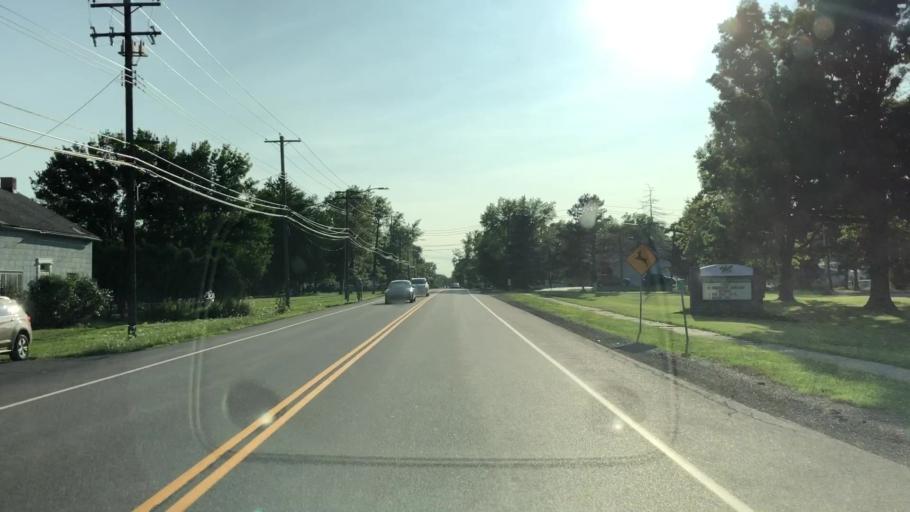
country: US
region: New York
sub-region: Erie County
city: Cheektowaga
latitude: 42.8571
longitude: -78.7317
